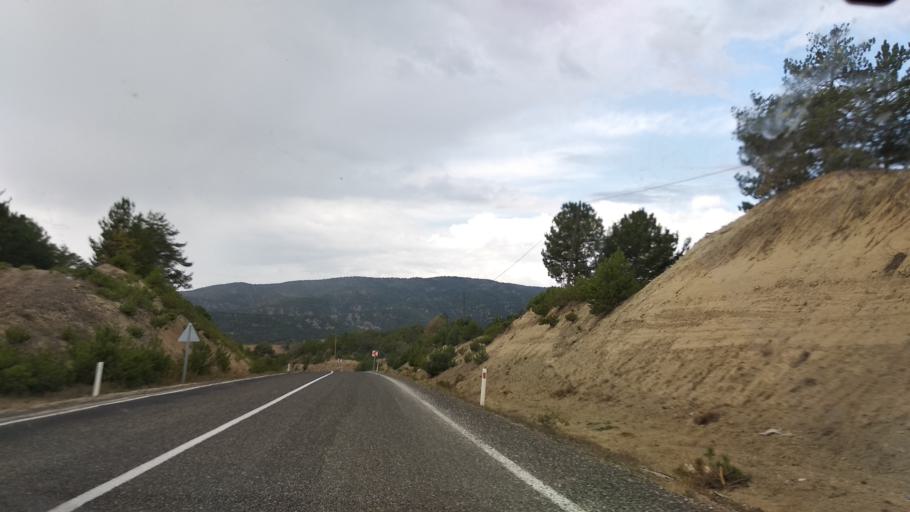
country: TR
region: Bolu
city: Seben
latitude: 40.3374
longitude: 31.4333
